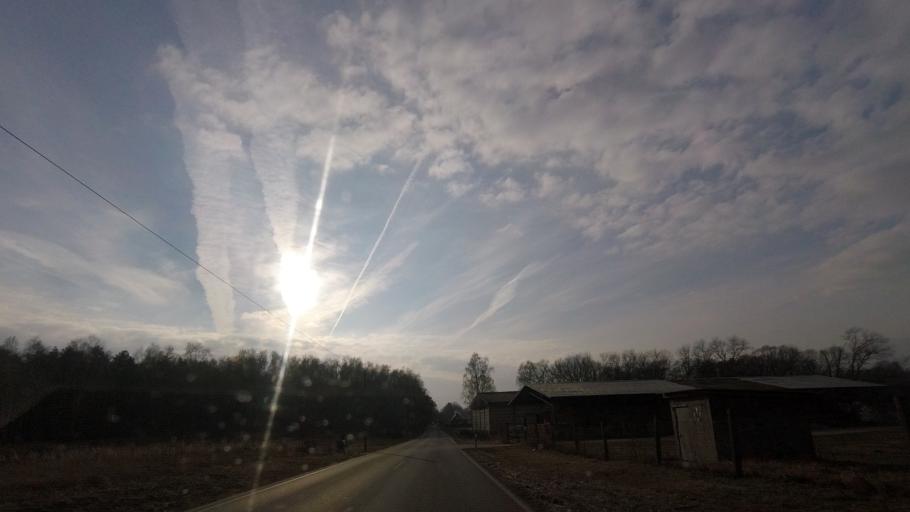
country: DE
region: Brandenburg
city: Belzig
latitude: 52.1330
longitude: 12.6393
